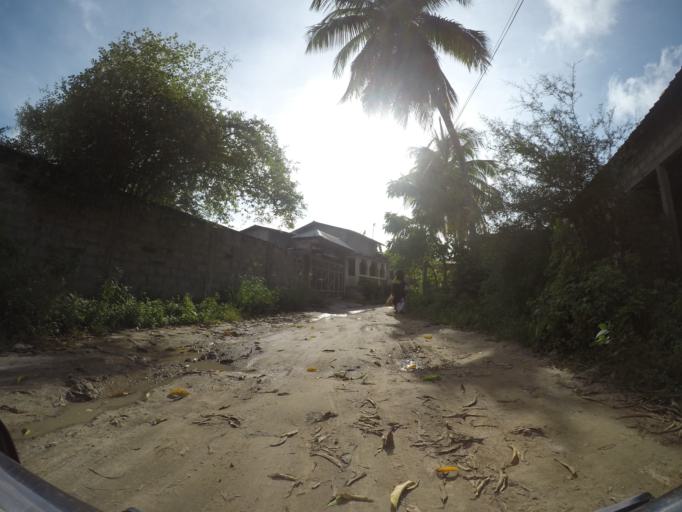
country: TZ
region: Pemba South
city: Chake Chake
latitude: -5.2265
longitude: 39.7764
